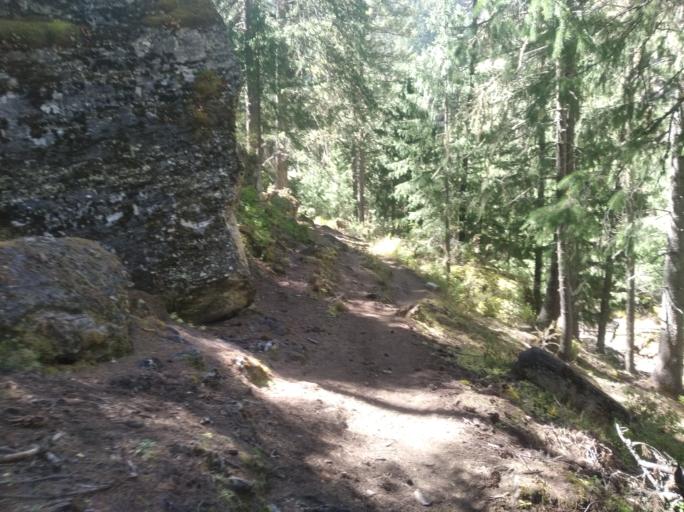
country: NP
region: Western Region
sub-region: Dhawalagiri Zone
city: Jomsom
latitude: 28.8839
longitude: 83.0634
